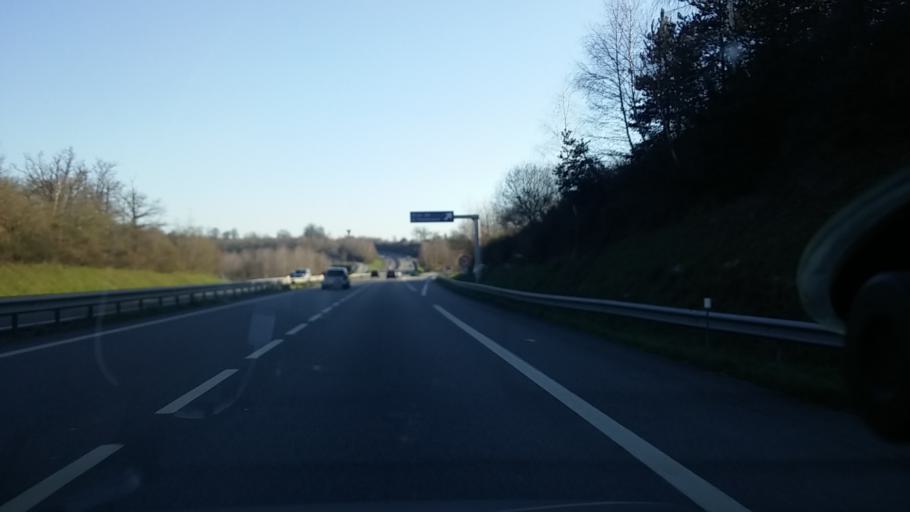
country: FR
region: Limousin
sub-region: Departement de la Haute-Vienne
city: Bessines-sur-Gartempe
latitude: 46.1641
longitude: 1.3769
